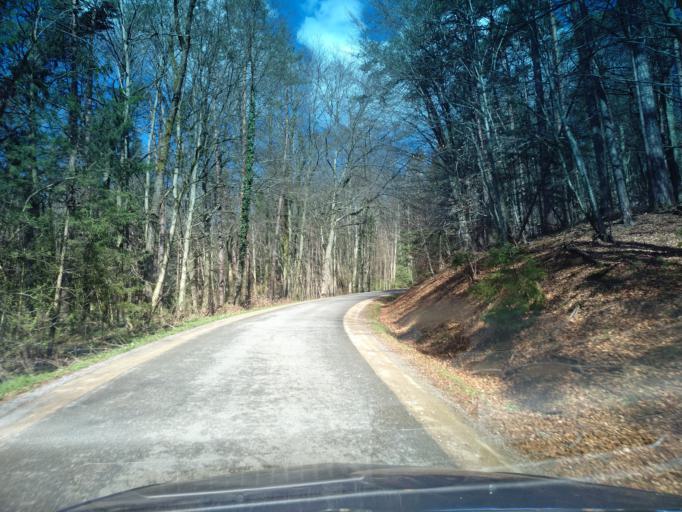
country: AT
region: Styria
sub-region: Politischer Bezirk Leibnitz
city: Sankt Johann im Saggautal
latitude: 46.7148
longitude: 15.3874
